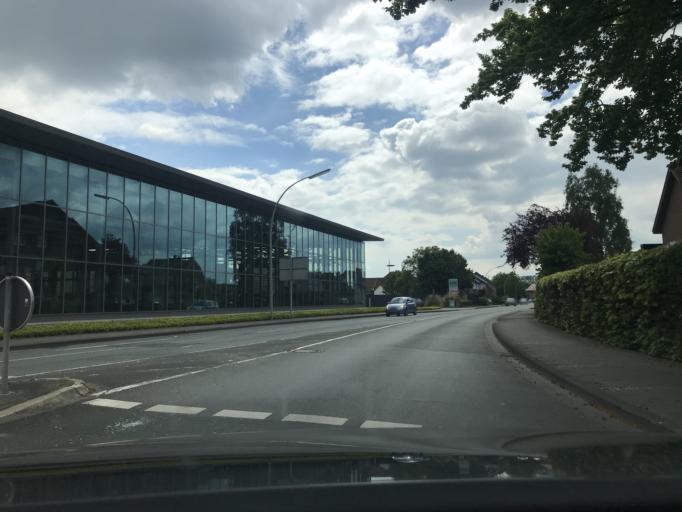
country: DE
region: North Rhine-Westphalia
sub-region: Regierungsbezirk Detmold
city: Rheda-Wiedenbruck
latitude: 51.8598
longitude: 8.2785
